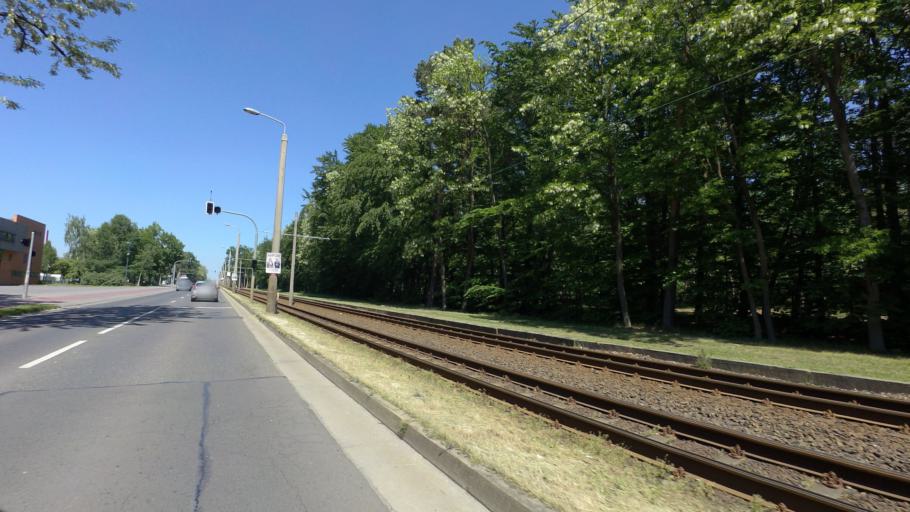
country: DE
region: Brandenburg
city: Cottbus
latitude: 51.7330
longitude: 14.3387
